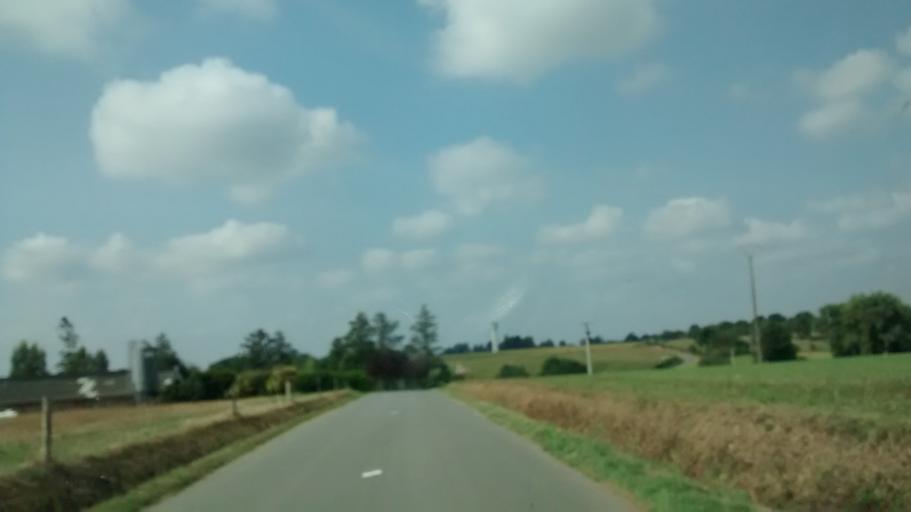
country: FR
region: Brittany
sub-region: Departement d'Ille-et-Vilaine
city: Livre-sur-Changeon
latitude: 48.2257
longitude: -1.2717
